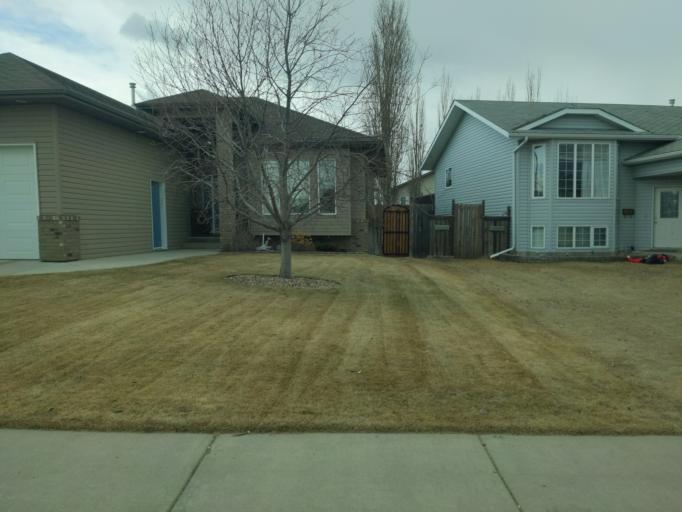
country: CA
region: Saskatchewan
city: Lloydminster
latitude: 53.2675
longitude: -110.0424
